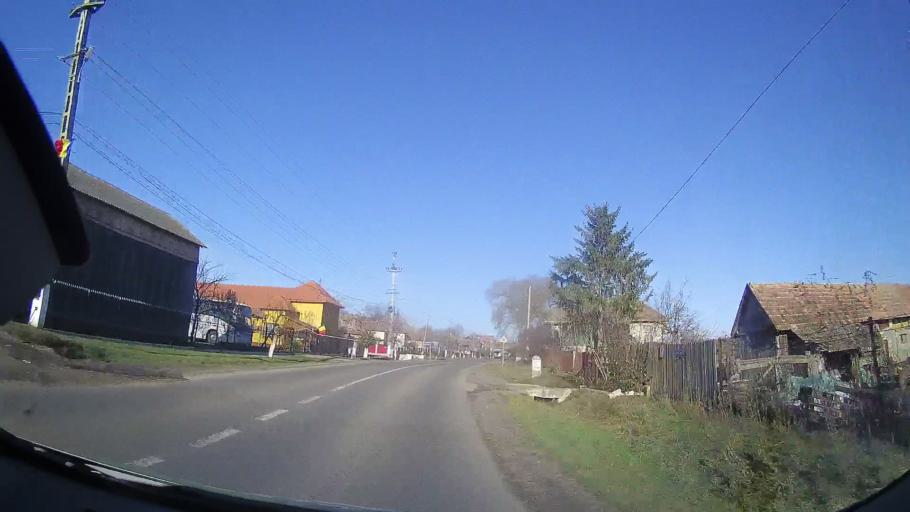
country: RO
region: Mures
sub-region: Comuna Sarmasu
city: Balda
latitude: 46.7236
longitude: 24.1432
